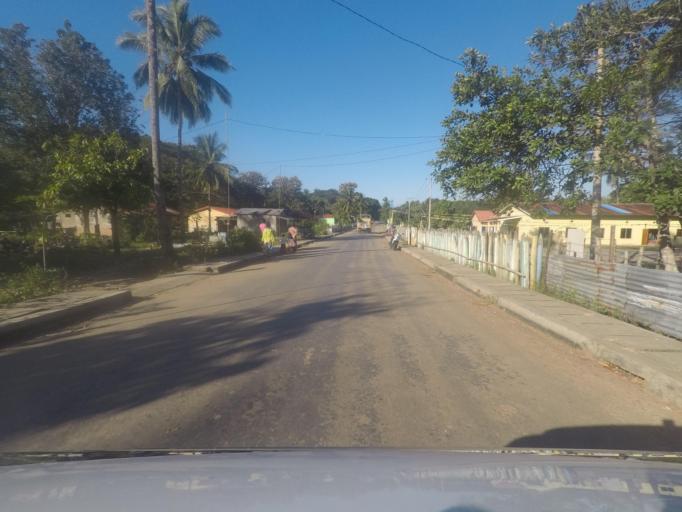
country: TL
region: Lautem
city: Lospalos
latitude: -8.3999
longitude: 127.1849
